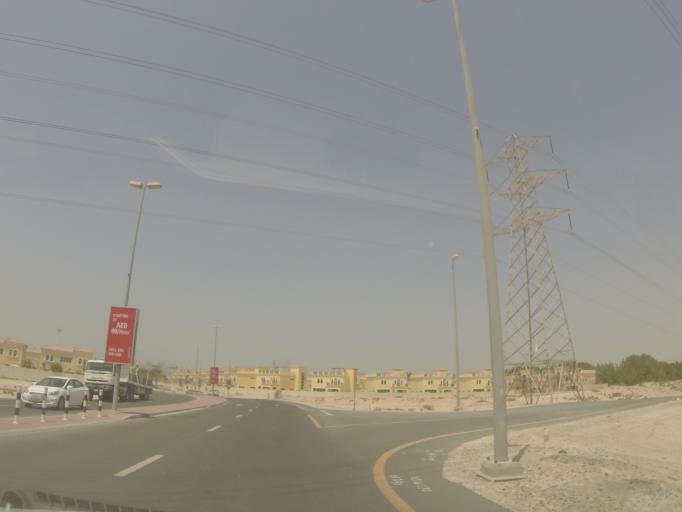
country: AE
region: Dubai
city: Dubai
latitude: 25.0403
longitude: 55.1715
